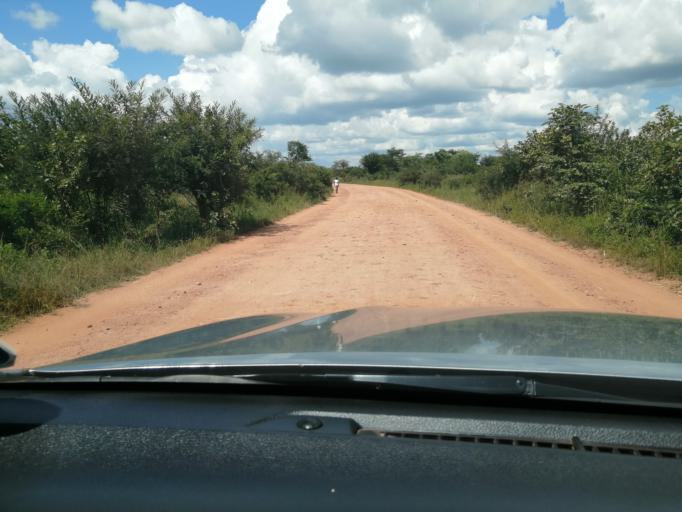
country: ZM
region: Lusaka
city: Lusaka
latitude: -15.1940
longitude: 27.9708
